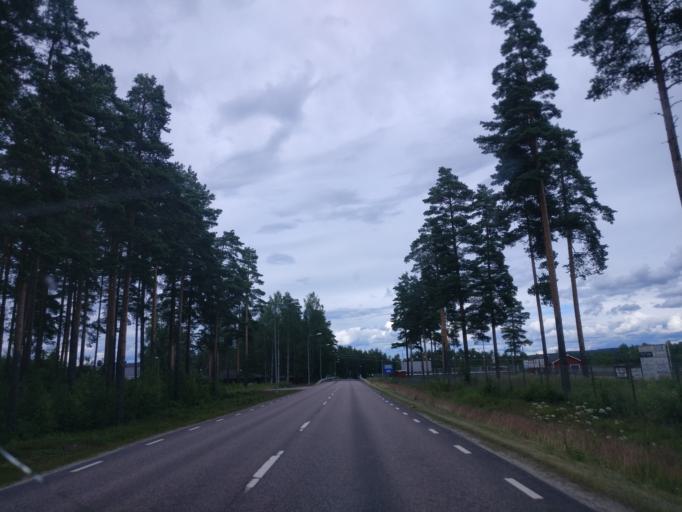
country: SE
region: Vaermland
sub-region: Hagfors Kommun
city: Ekshaerad
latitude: 60.1706
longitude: 13.4834
